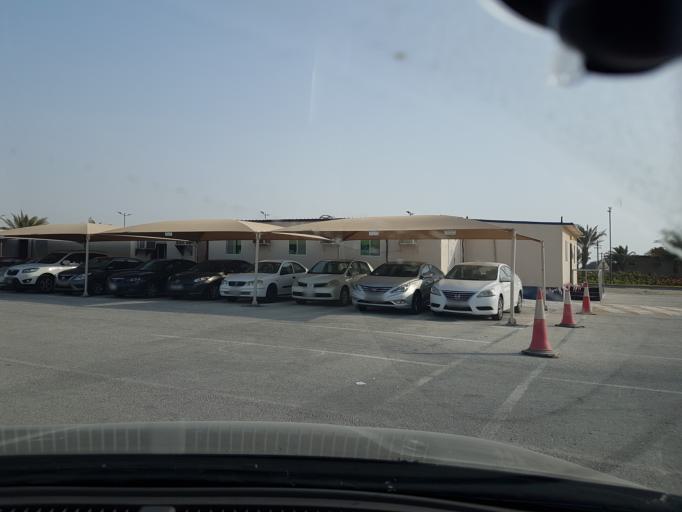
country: BH
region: Northern
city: Ar Rifa'
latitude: 26.0910
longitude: 50.5514
